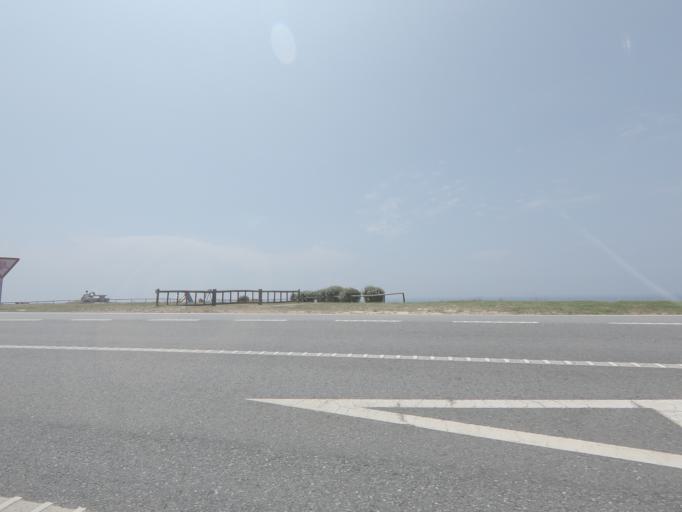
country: ES
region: Galicia
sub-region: Provincia de Pontevedra
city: A Guarda
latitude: 41.9137
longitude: -8.8793
